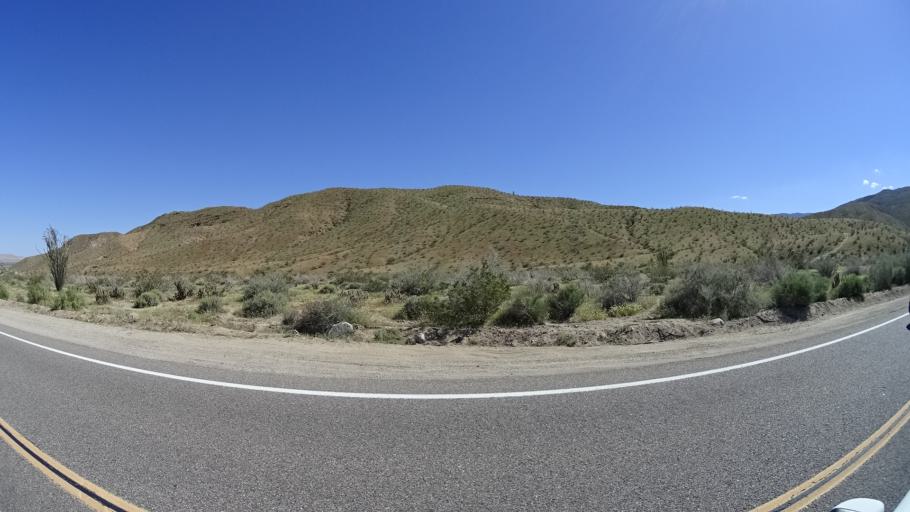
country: US
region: California
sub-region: San Diego County
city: Borrego Springs
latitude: 33.2523
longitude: -116.4007
